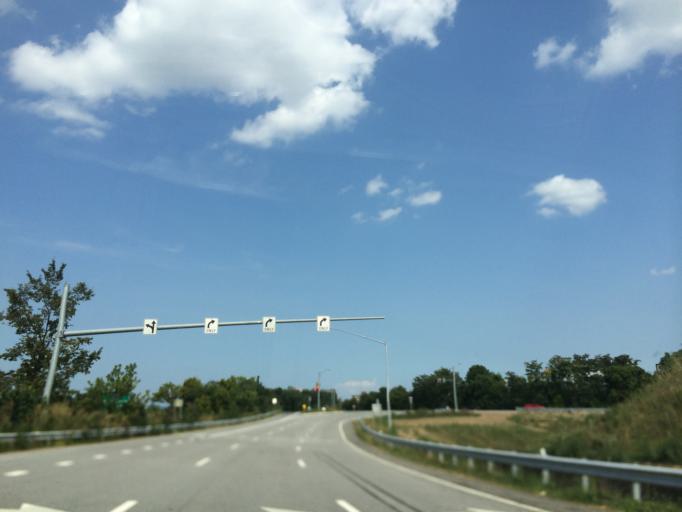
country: US
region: Maryland
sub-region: Anne Arundel County
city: Linthicum
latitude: 39.2114
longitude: -76.6803
